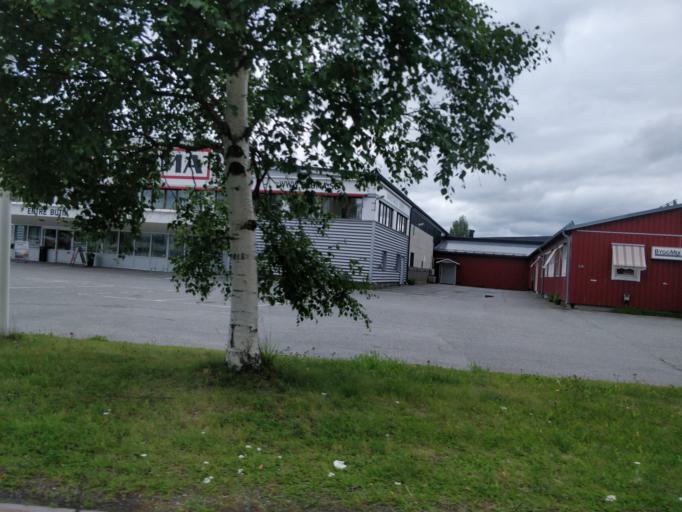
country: SE
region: Vaesterbotten
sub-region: Skelleftea Kommun
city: Viken
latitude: 64.7594
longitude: 20.8895
